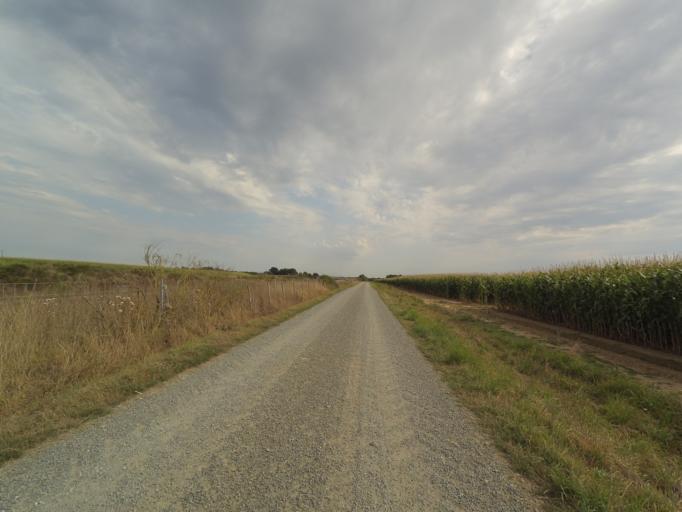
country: FR
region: Pays de la Loire
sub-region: Departement de la Vendee
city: Bouffere
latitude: 46.9758
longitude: -1.3709
